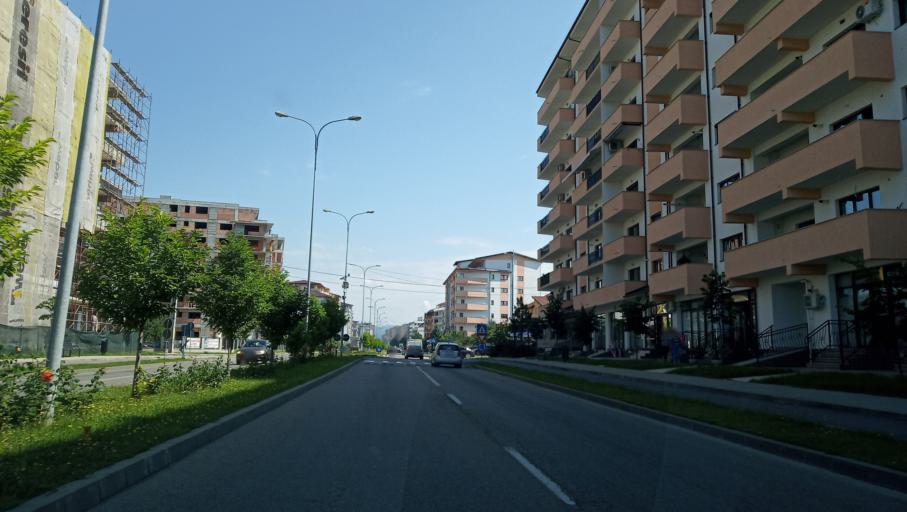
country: RO
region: Valcea
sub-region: Municipiul Ramnicu Valcea
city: Ramnicu Valcea
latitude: 45.0839
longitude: 24.3674
